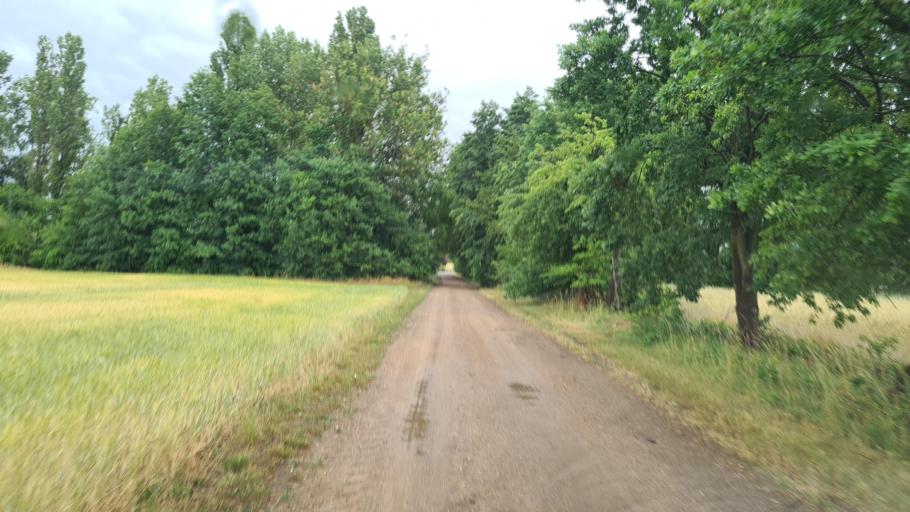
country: DE
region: Brandenburg
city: Bad Liebenwerda
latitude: 51.4946
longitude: 13.3290
